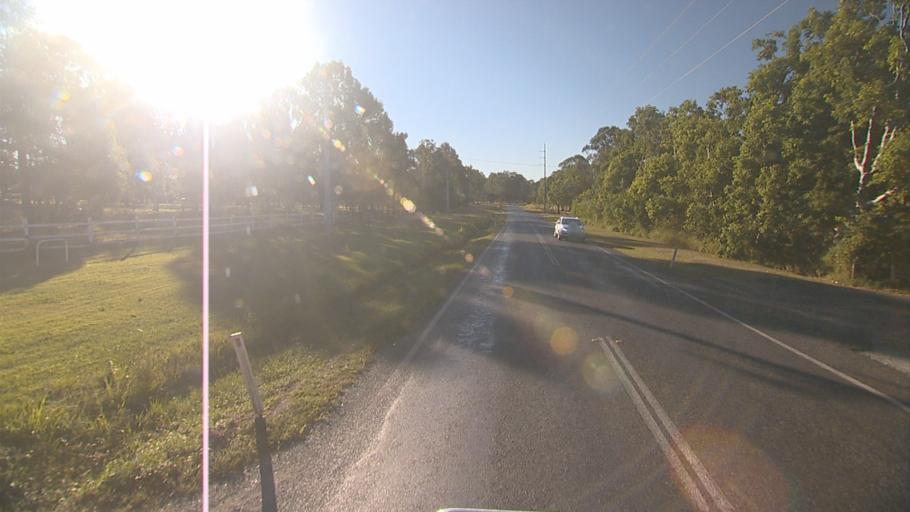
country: AU
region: Queensland
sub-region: Logan
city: Chambers Flat
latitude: -27.7434
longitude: 153.0878
